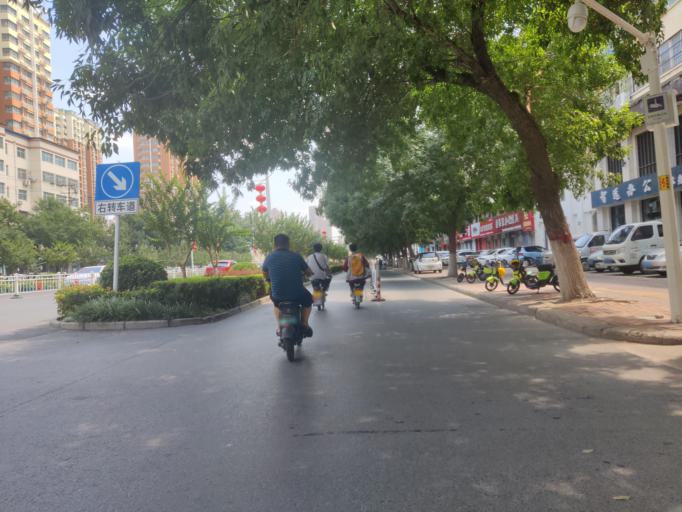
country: CN
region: Henan Sheng
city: Puyang
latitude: 35.7723
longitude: 115.0242
